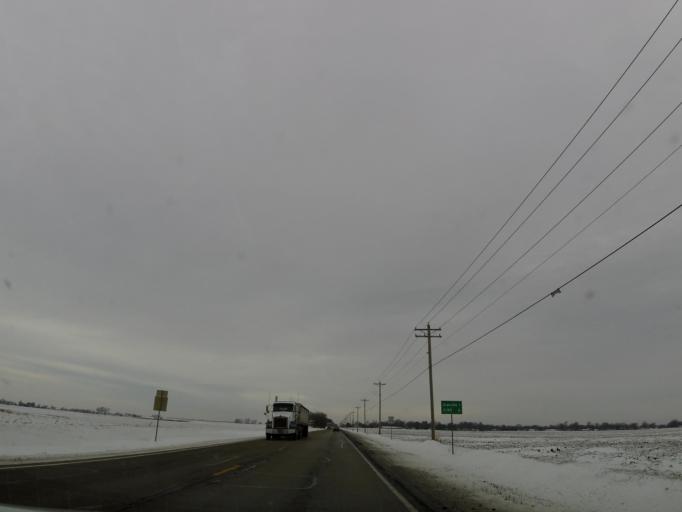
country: US
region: Illinois
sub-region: Putnam County
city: Granville
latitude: 41.2578
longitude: -89.2041
